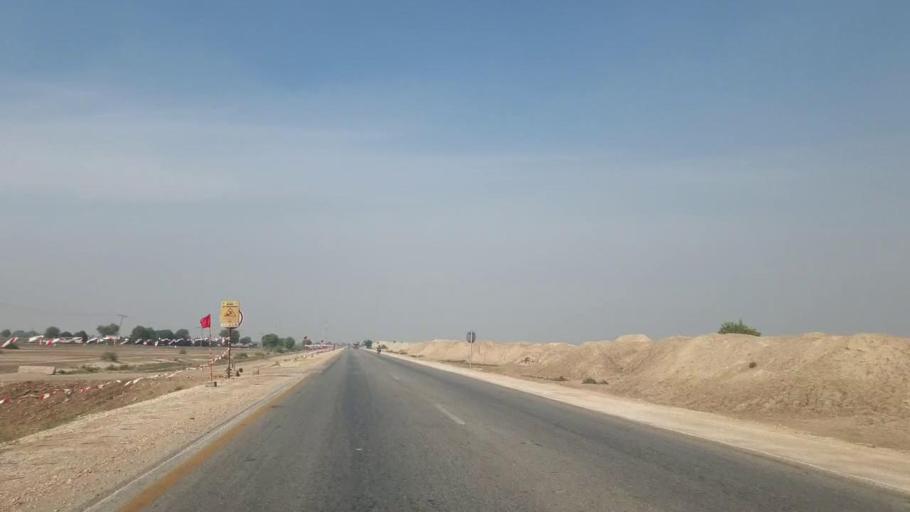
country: PK
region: Sindh
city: Sann
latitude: 25.9696
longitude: 68.1887
